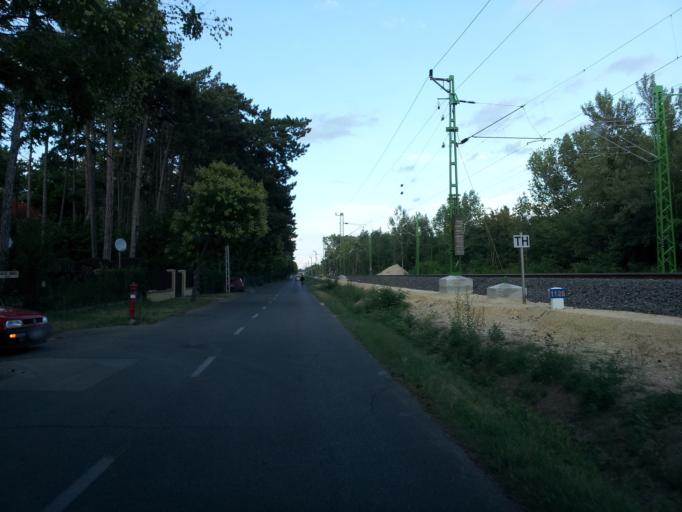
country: HU
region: Somogy
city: Siofok
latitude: 46.9161
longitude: 18.0764
